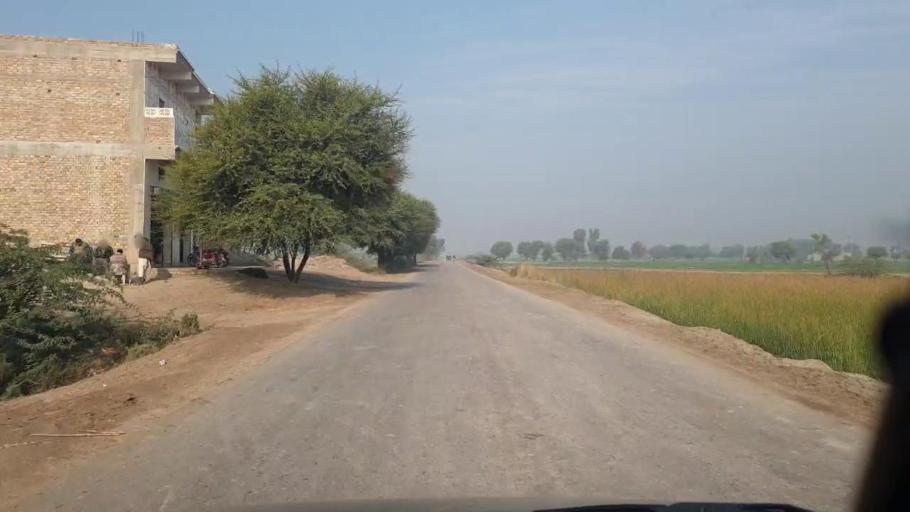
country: PK
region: Sindh
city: Shahdadpur
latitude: 25.9395
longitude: 68.6031
